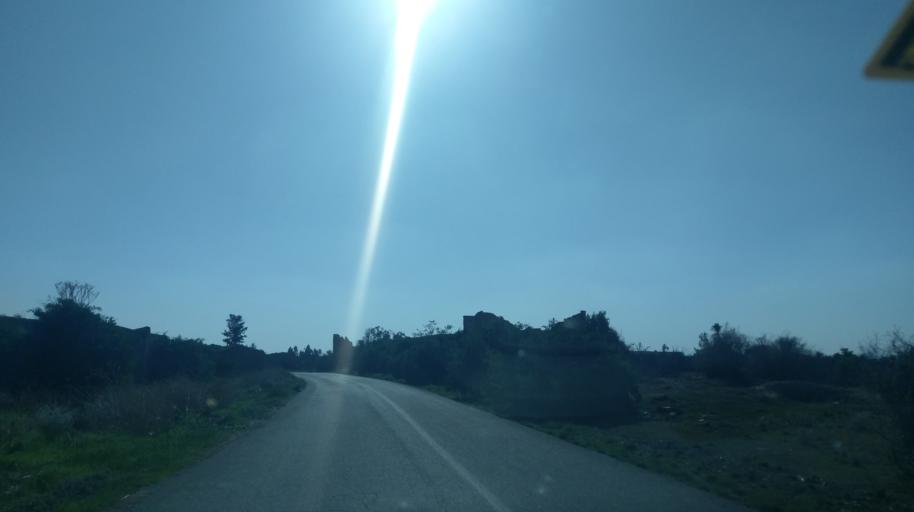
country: CY
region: Larnaka
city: Athienou
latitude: 35.0788
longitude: 33.4907
